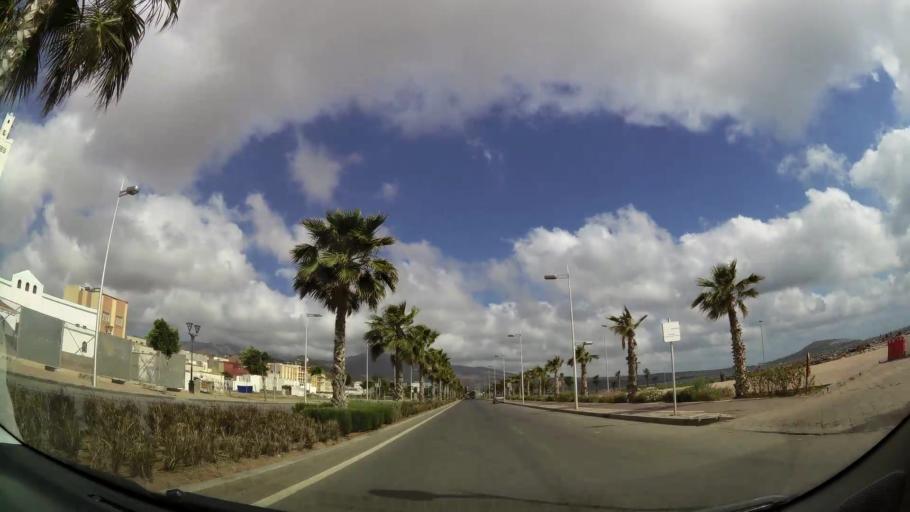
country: MA
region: Oriental
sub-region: Nador
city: Nador
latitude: 35.1726
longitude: -2.9166
